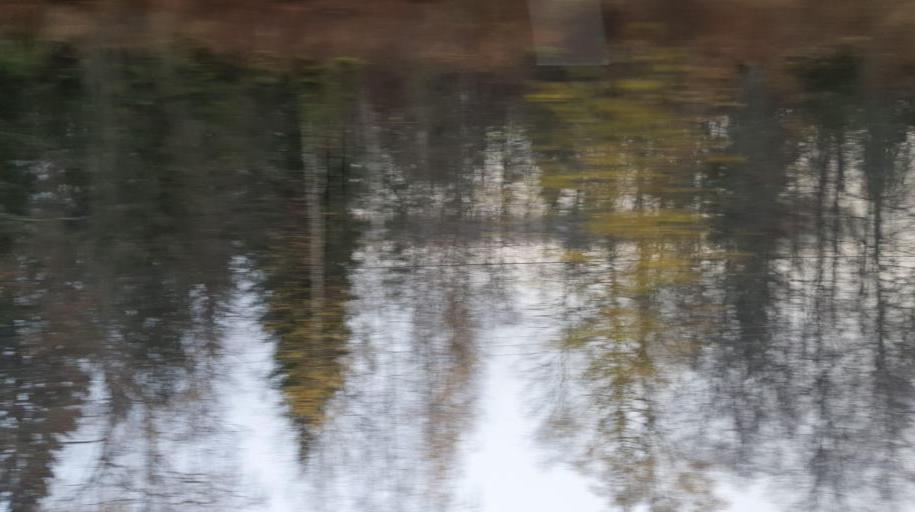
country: NO
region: Buskerud
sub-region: Krodsherad
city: Noresund
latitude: 60.1464
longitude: 9.7646
